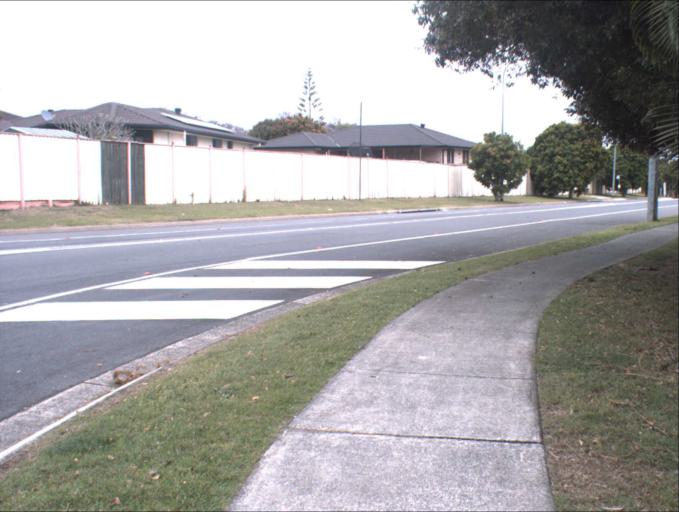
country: AU
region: Queensland
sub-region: Logan
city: Park Ridge South
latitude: -27.6806
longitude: 153.0439
